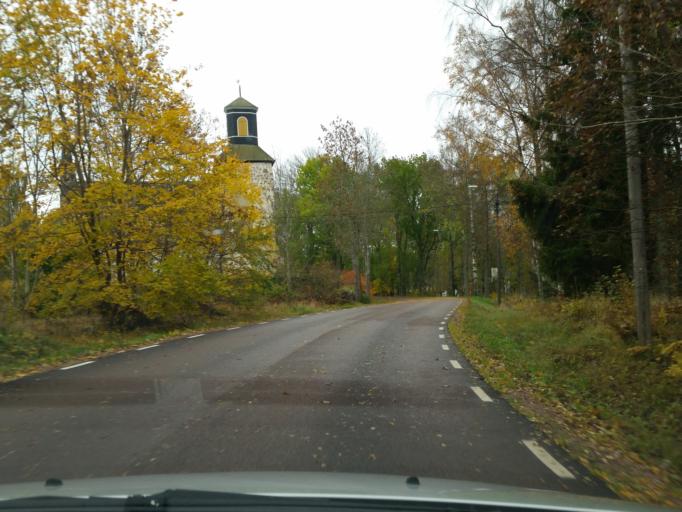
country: AX
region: Alands landsbygd
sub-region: Lemland
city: Lemland
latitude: 60.0758
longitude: 20.0834
